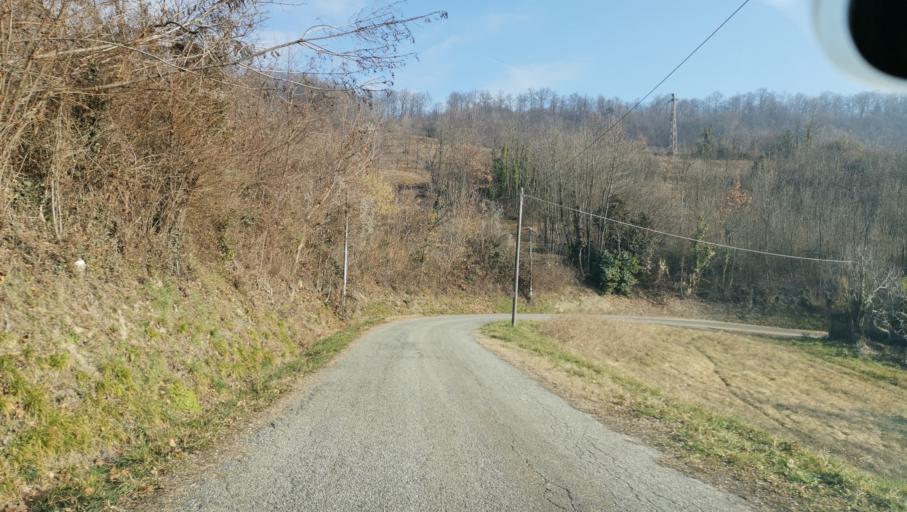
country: IT
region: Piedmont
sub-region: Provincia di Torino
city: Rivalba
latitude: 45.1341
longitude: 7.8906
